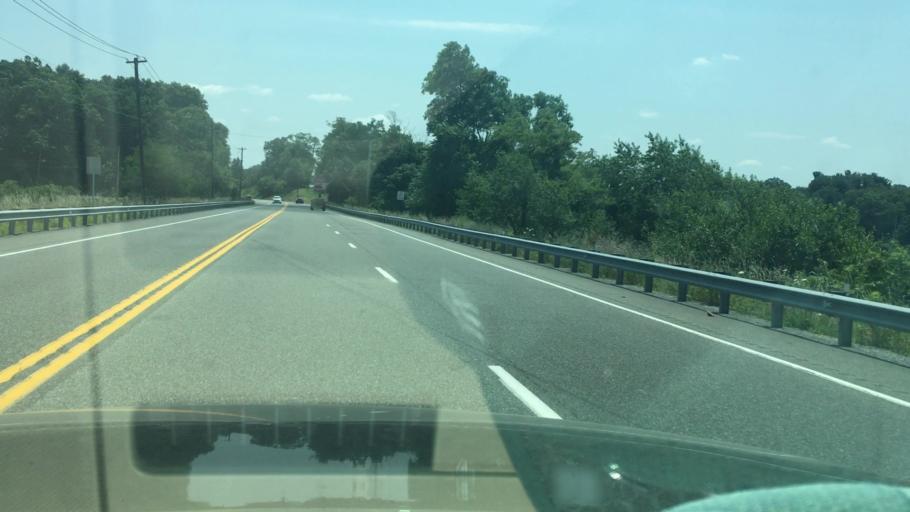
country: US
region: Pennsylvania
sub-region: Lehigh County
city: Schnecksville
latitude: 40.6179
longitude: -75.6595
